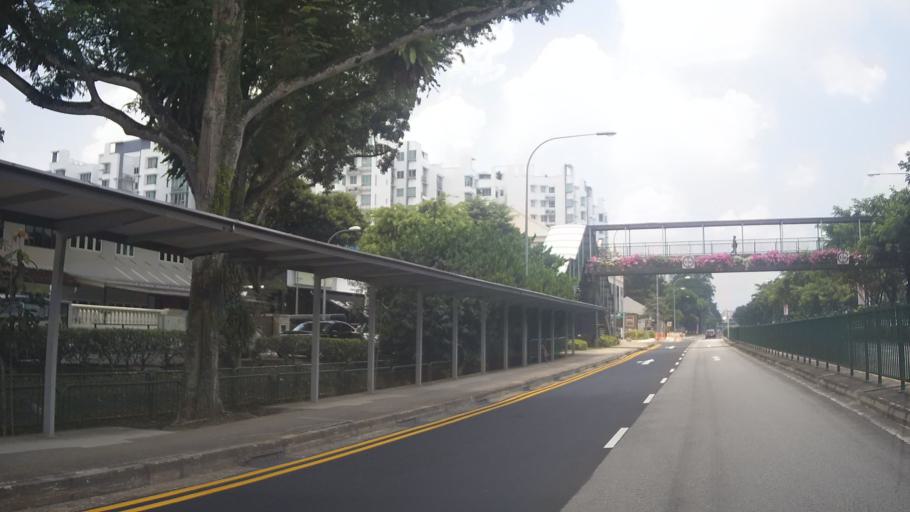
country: SG
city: Singapore
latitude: 1.3329
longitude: 103.7918
